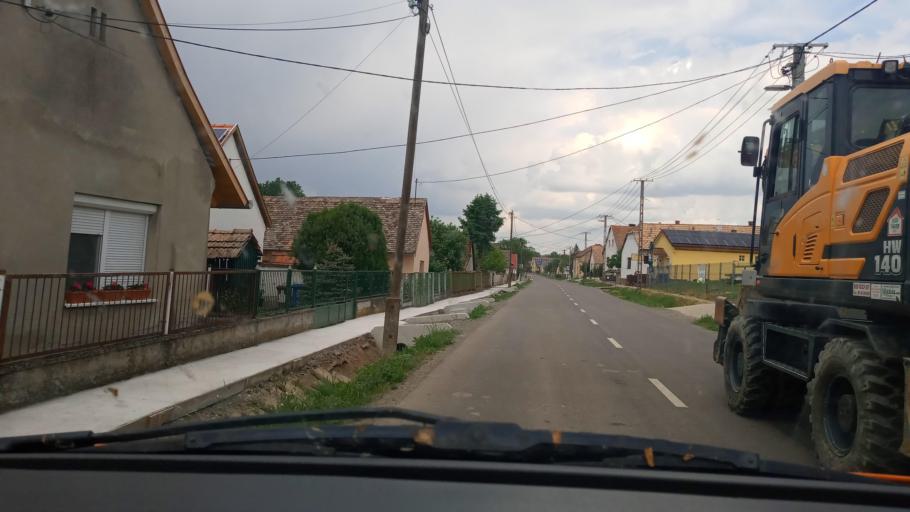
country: HU
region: Baranya
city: Villany
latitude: 45.8474
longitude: 18.4848
